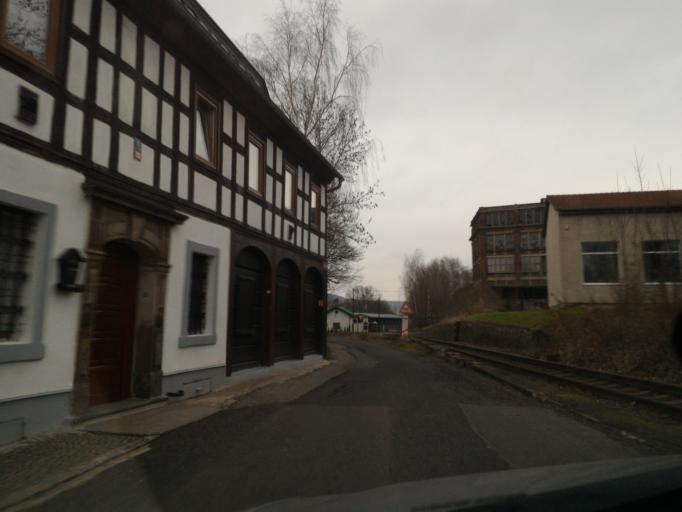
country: CZ
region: Ustecky
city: Varnsdorf
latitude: 50.9015
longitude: 14.6297
